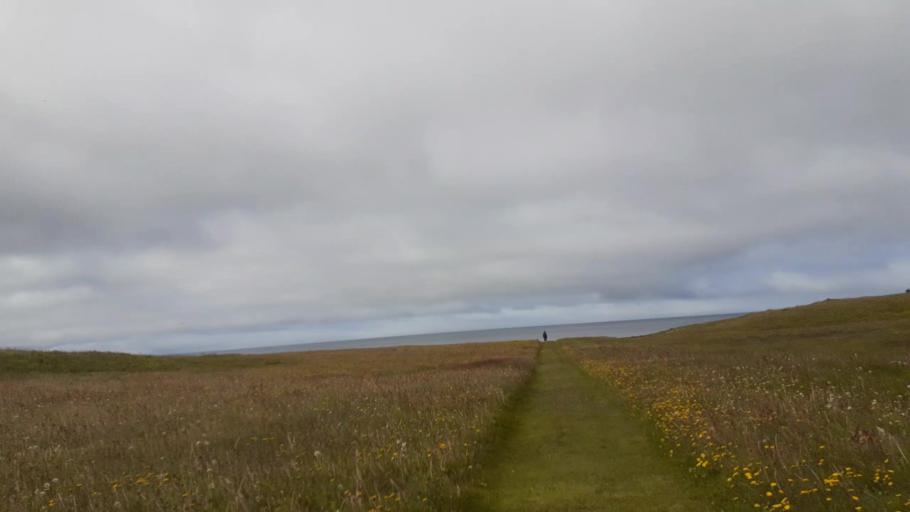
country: IS
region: Northeast
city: Dalvik
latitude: 66.5491
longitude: -18.0234
